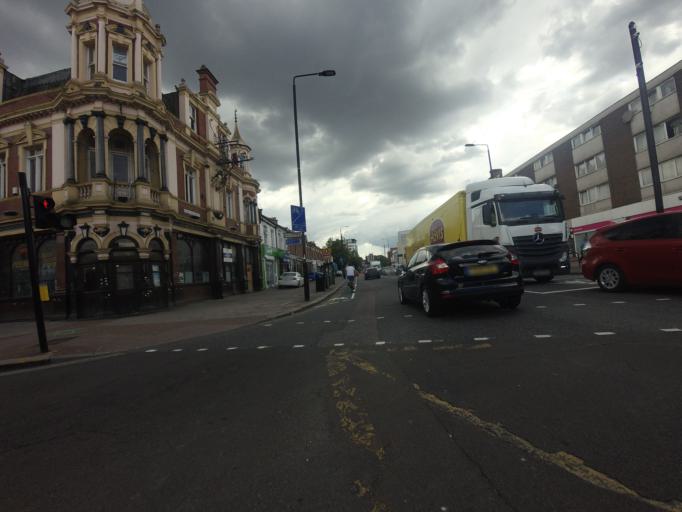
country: GB
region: England
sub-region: Greater London
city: East Ham
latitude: 51.5506
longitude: 0.0474
